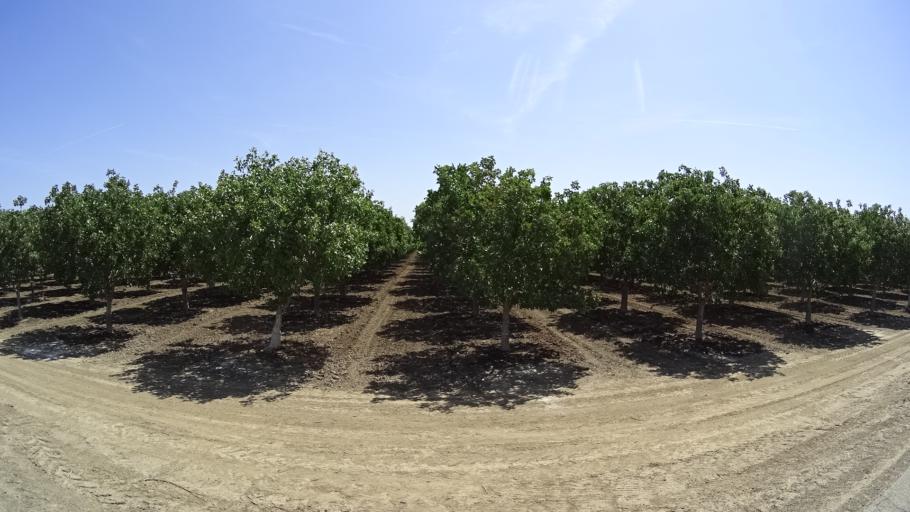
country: US
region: California
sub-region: Kings County
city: Kettleman City
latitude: 36.1059
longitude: -120.0037
